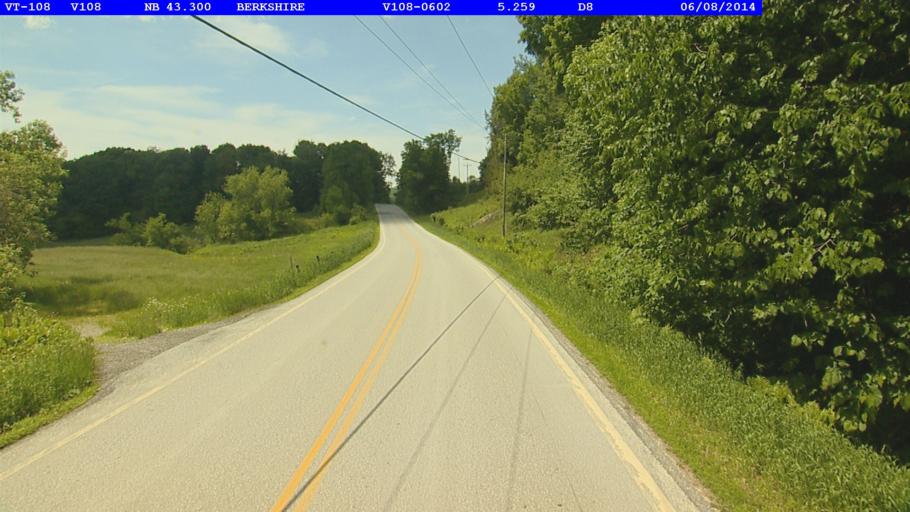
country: US
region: Vermont
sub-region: Franklin County
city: Enosburg Falls
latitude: 44.9945
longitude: -72.8185
